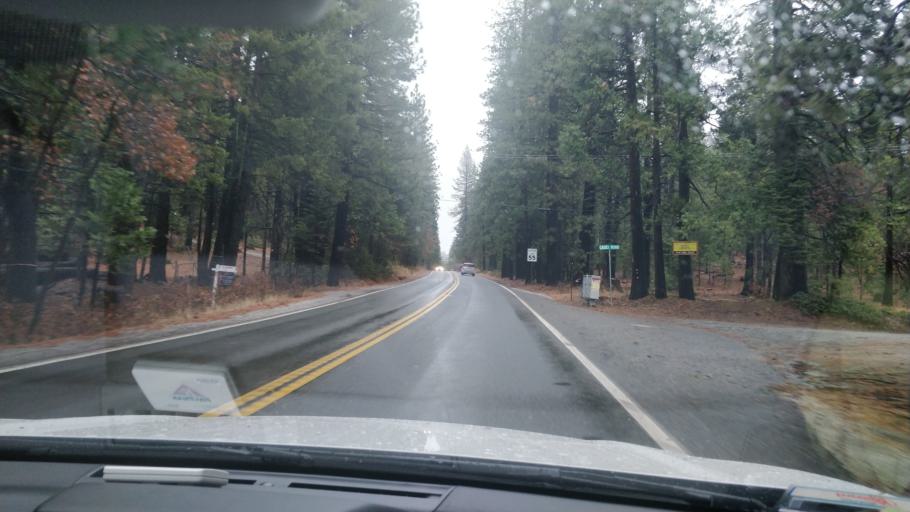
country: US
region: California
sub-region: Nevada County
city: Nevada City
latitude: 39.3181
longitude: -120.8898
